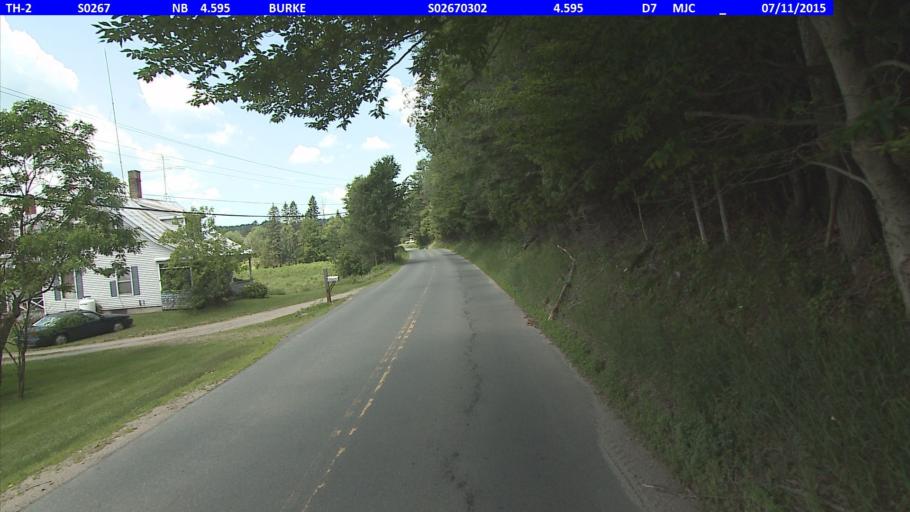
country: US
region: Vermont
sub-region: Caledonia County
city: Lyndonville
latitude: 44.6391
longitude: -71.9743
